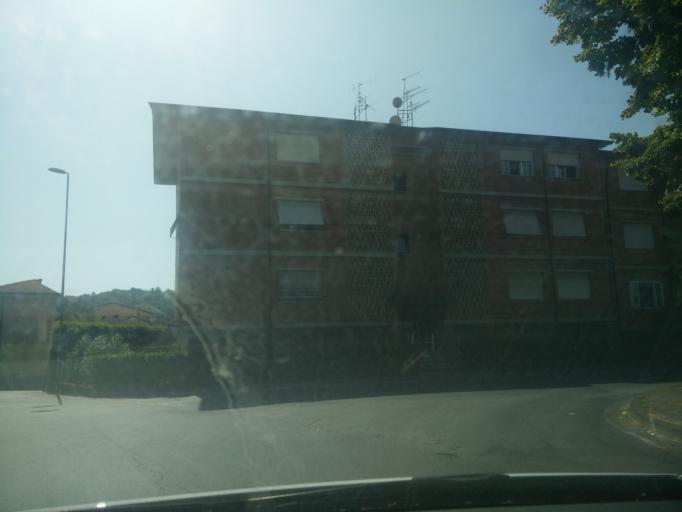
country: IT
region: Tuscany
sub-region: Provincia di Massa-Carrara
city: Carrara
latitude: 44.0602
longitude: 10.0847
